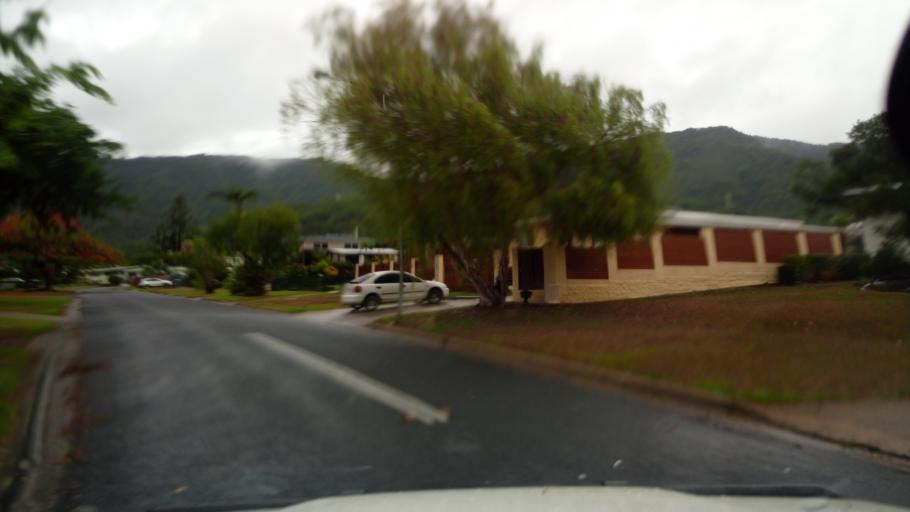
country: AU
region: Queensland
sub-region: Cairns
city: Woree
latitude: -16.9552
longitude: 145.7302
